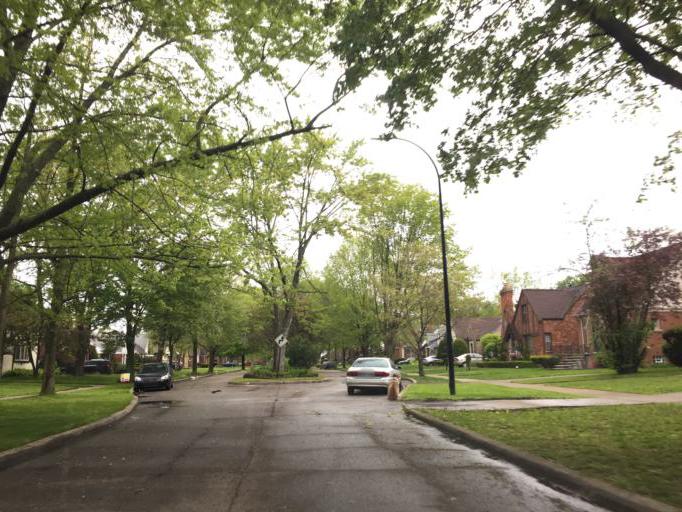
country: US
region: Michigan
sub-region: Wayne County
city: Redford
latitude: 42.3964
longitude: -83.2300
